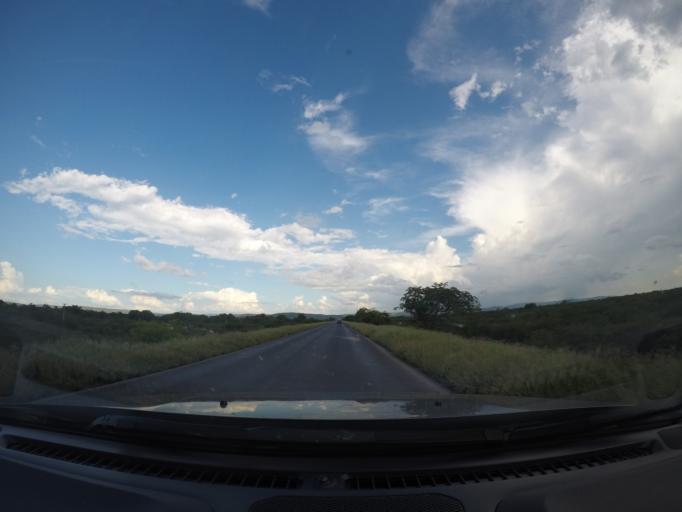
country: BR
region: Bahia
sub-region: Ibotirama
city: Ibotirama
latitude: -12.1746
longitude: -43.2544
